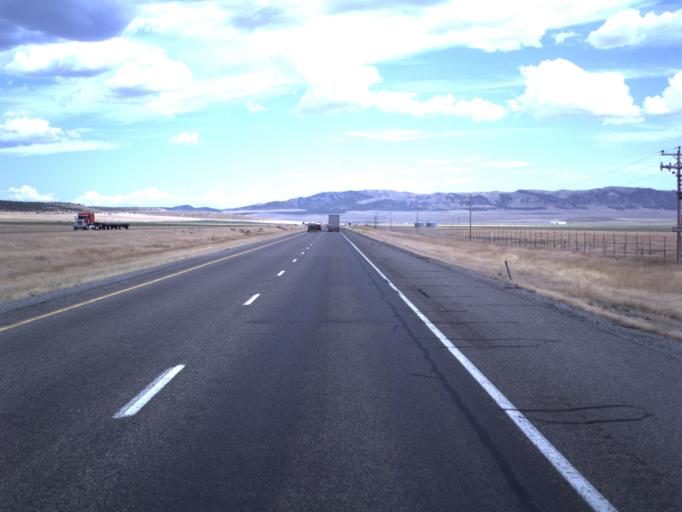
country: US
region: Idaho
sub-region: Oneida County
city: Malad City
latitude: 41.9857
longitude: -112.8144
